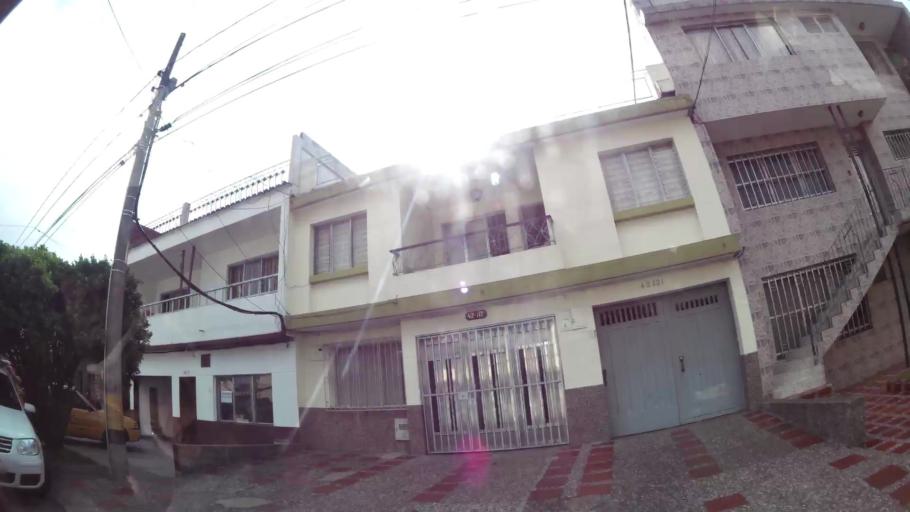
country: CO
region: Antioquia
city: Medellin
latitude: 6.2476
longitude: -75.5850
